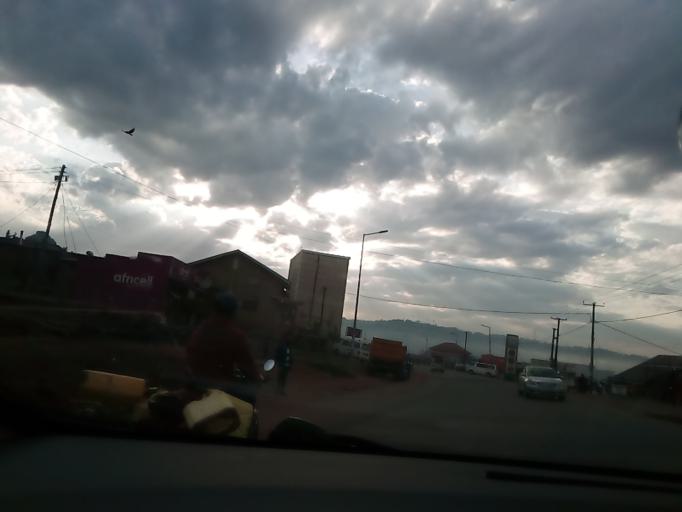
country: UG
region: Central Region
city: Masaka
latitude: -0.3398
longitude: 31.7051
